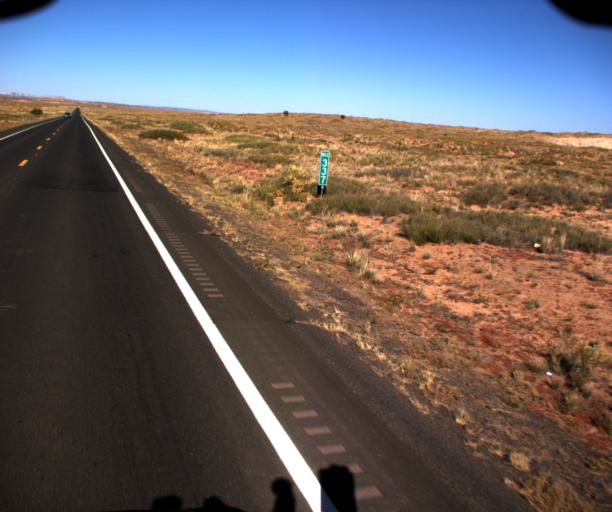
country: US
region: Arizona
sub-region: Coconino County
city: Tuba City
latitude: 36.2492
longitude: -111.0224
